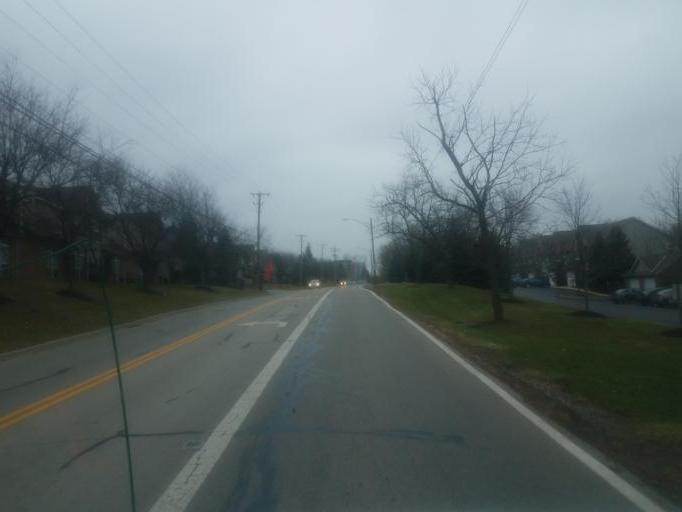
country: US
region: Ohio
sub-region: Franklin County
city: Huber Ridge
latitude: 40.0987
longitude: -82.9365
